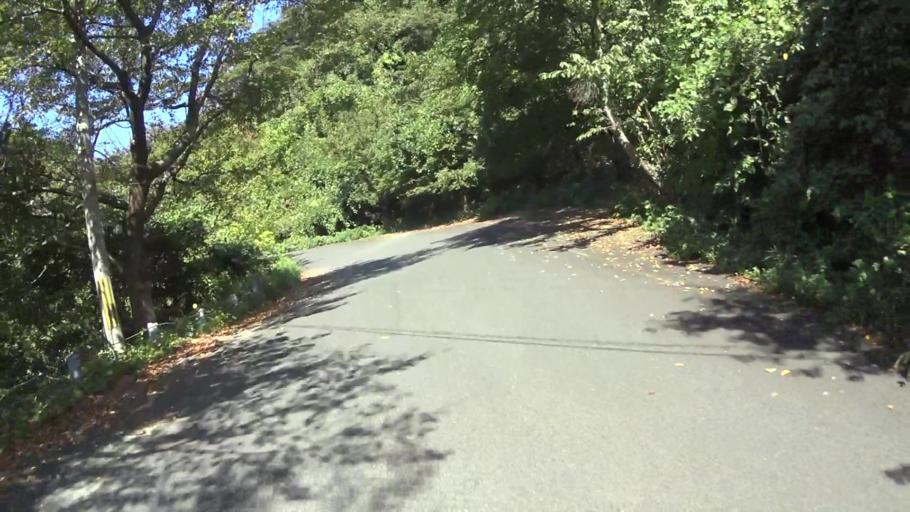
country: JP
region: Kyoto
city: Miyazu
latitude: 35.7706
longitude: 135.2262
